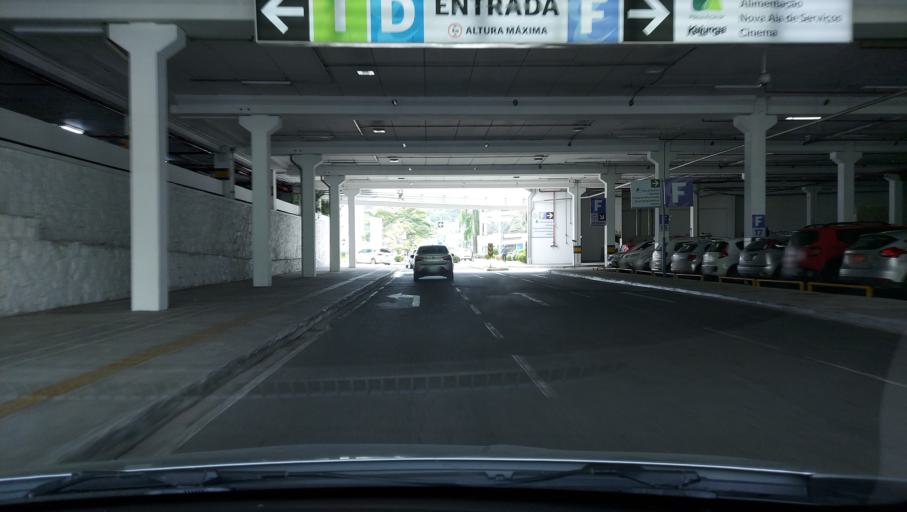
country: BR
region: Bahia
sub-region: Salvador
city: Salvador
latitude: -12.9829
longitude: -38.4638
